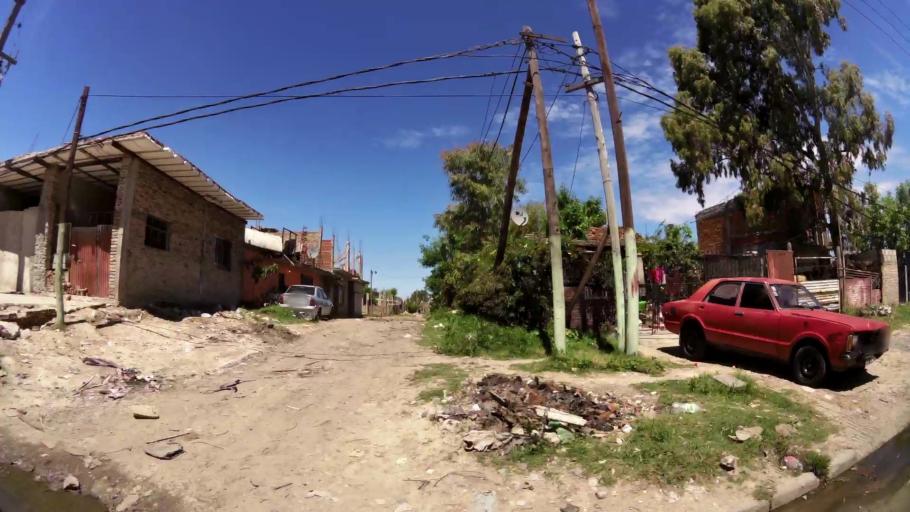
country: AR
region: Buenos Aires
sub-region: Partido de Quilmes
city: Quilmes
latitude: -34.7254
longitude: -58.3155
